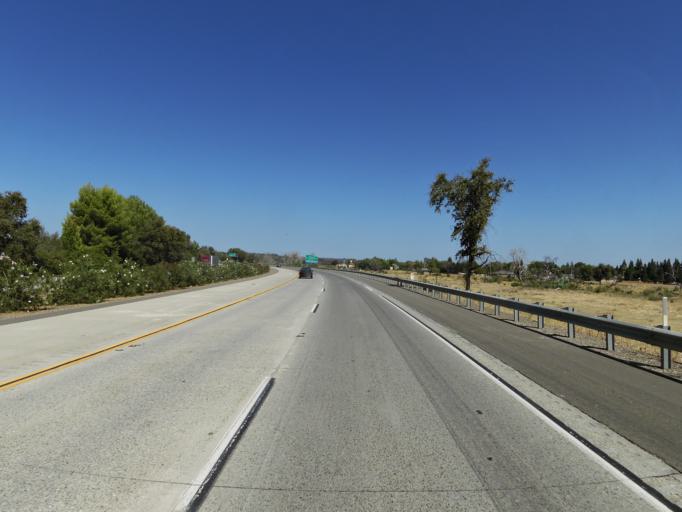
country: US
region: California
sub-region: Tehama County
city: Red Bluff
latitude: 40.1733
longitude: -122.2213
